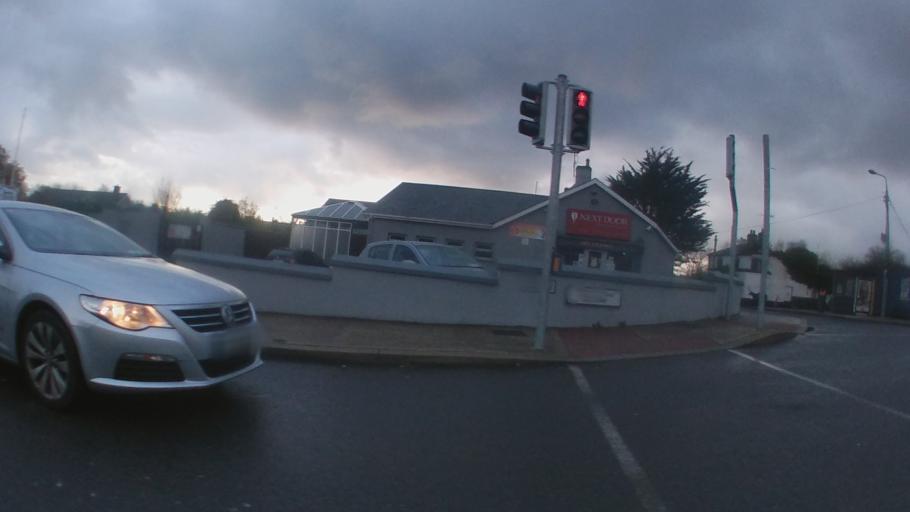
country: IE
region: Leinster
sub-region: Wicklow
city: Kilcoole
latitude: 53.1064
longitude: -6.0646
